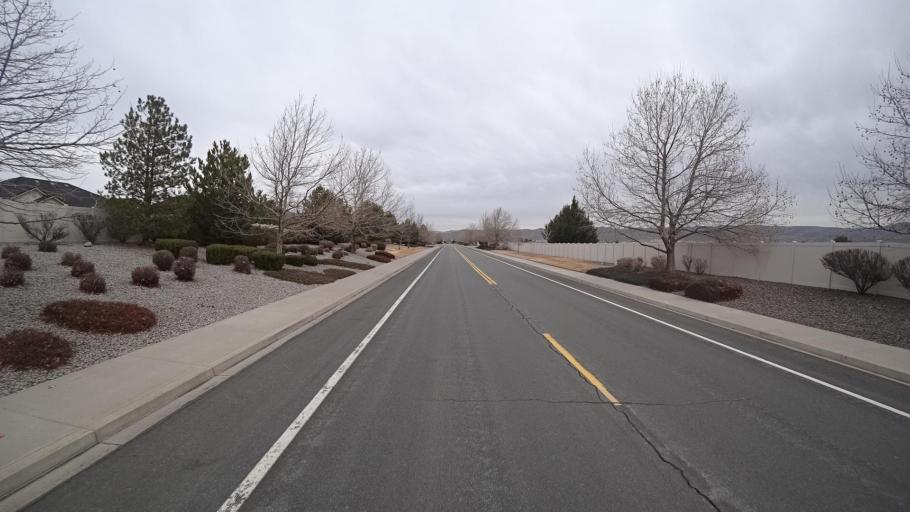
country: US
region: Nevada
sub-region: Washoe County
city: Spanish Springs
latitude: 39.6614
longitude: -119.7259
